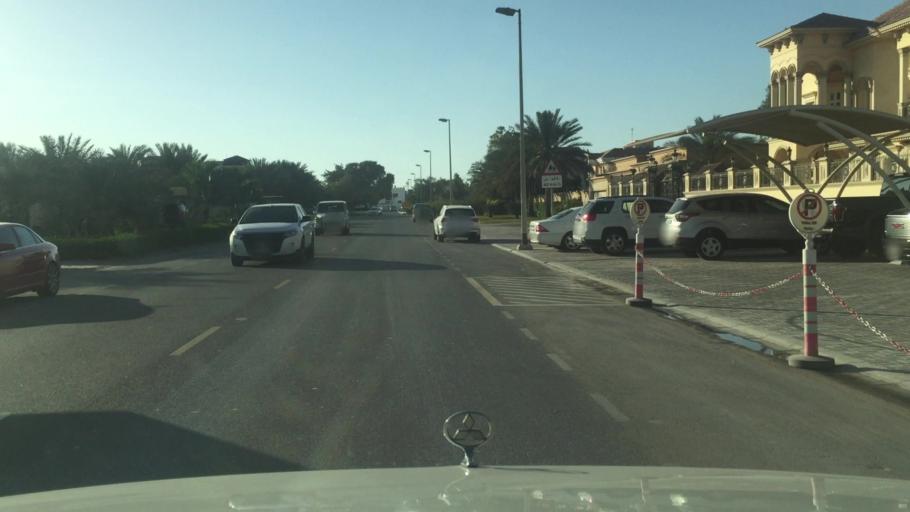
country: AE
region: Dubai
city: Dubai
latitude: 25.1612
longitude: 55.2298
